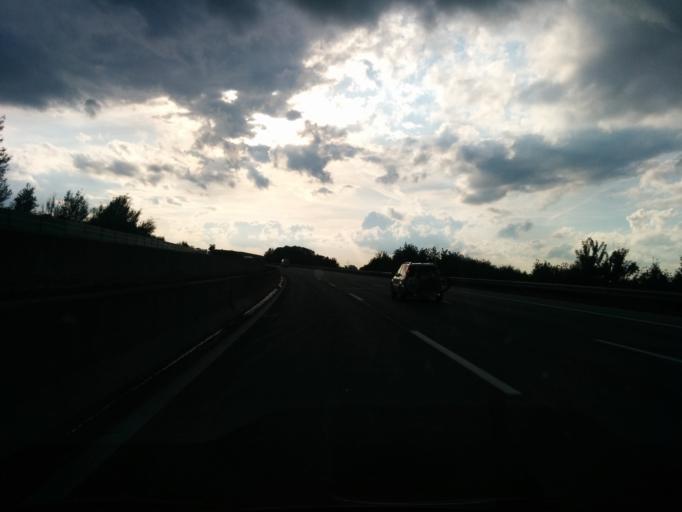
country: AT
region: Lower Austria
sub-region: Politischer Bezirk Amstetten
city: Strengberg
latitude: 48.1186
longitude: 14.6477
